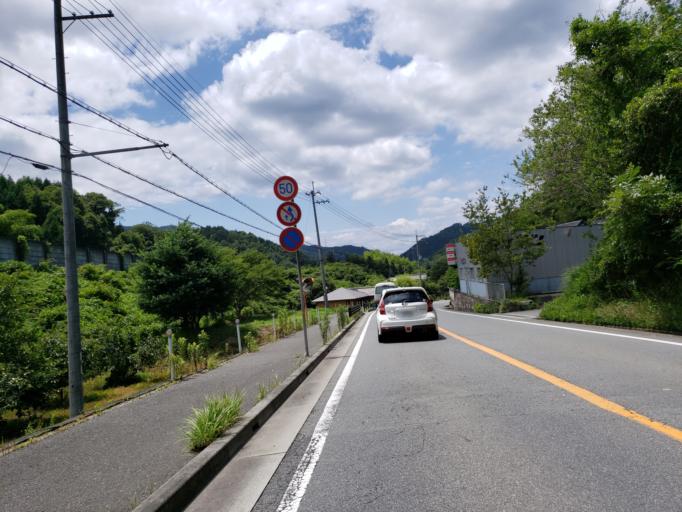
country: JP
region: Hyogo
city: Yamazakicho-nakabirose
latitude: 34.9760
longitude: 134.6430
